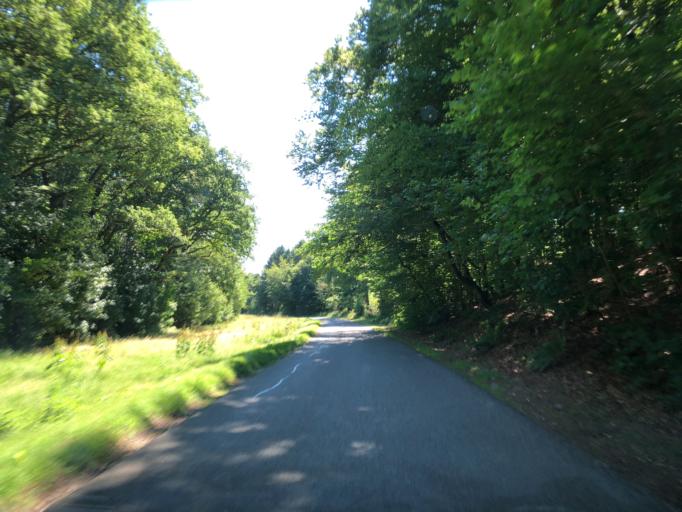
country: DK
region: Central Jutland
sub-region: Viborg Kommune
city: Viborg
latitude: 56.5142
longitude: 9.4980
